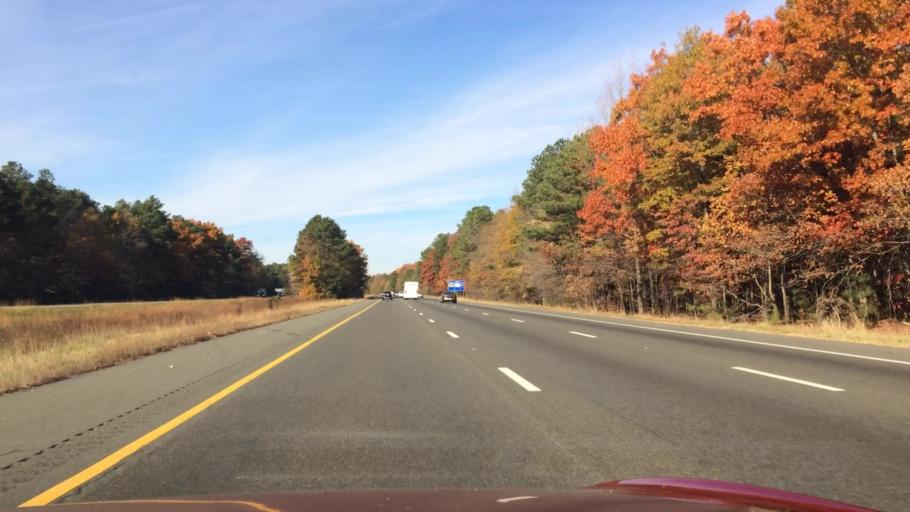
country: US
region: Virginia
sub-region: Henrico County
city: Glen Allen
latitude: 37.6794
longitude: -77.5116
